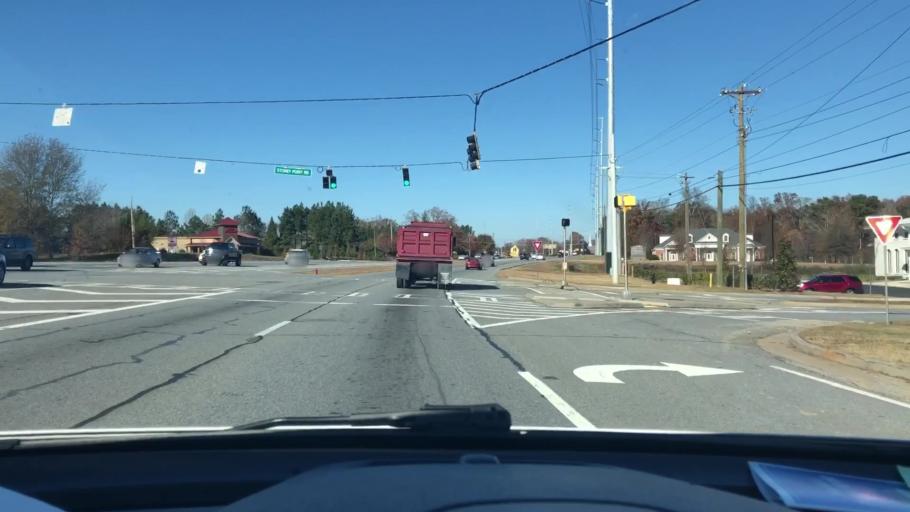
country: US
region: Georgia
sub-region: Forsyth County
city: Cumming
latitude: 34.1353
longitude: -84.1735
